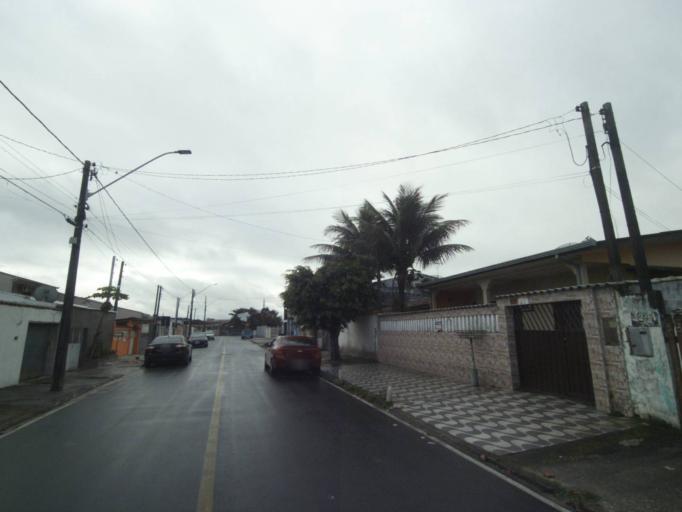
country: BR
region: Parana
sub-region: Paranagua
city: Paranagua
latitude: -25.5698
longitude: -48.5697
